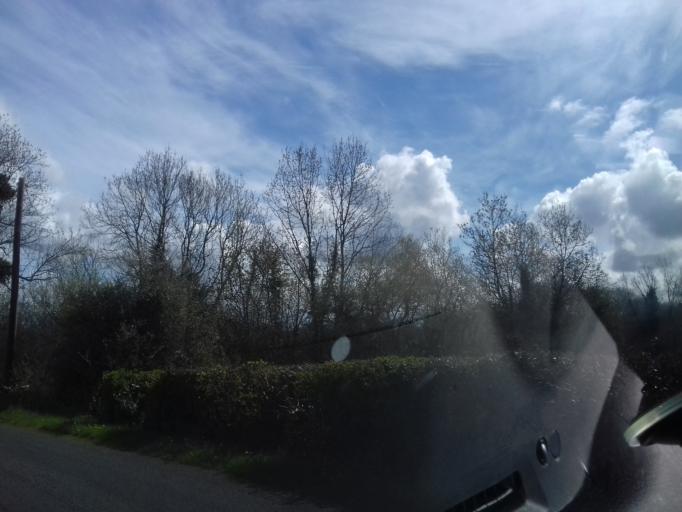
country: IE
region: Ulster
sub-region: An Cabhan
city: Belturbet
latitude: 54.1684
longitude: -7.5068
